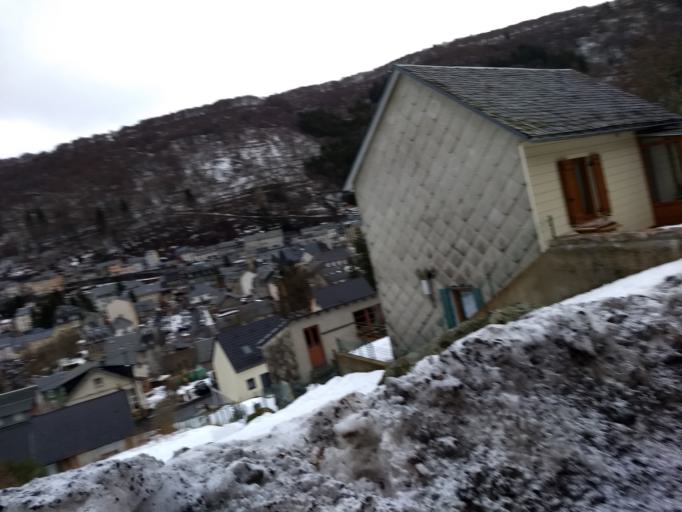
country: FR
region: Auvergne
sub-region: Departement du Puy-de-Dome
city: Mont-Dore
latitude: 45.5744
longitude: 2.8049
